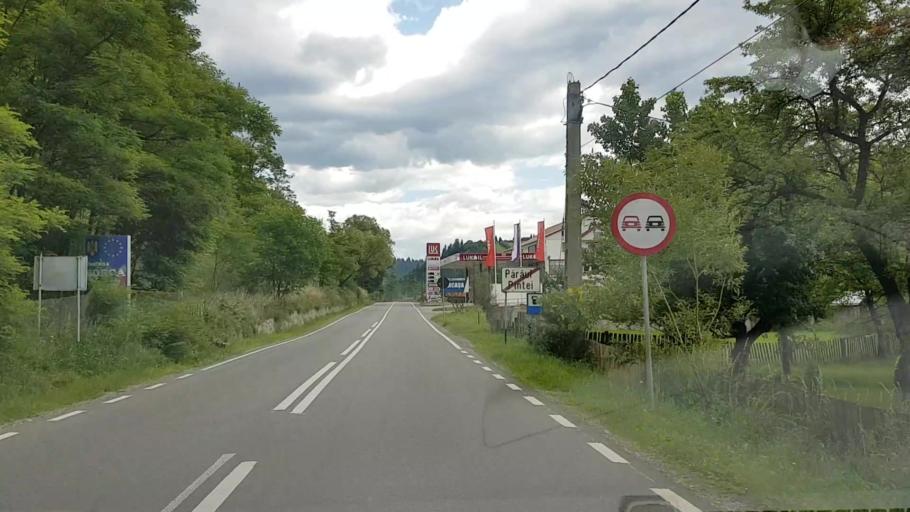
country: RO
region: Neamt
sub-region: Comuna Farcasa
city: Farcasa
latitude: 47.1606
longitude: 25.8207
